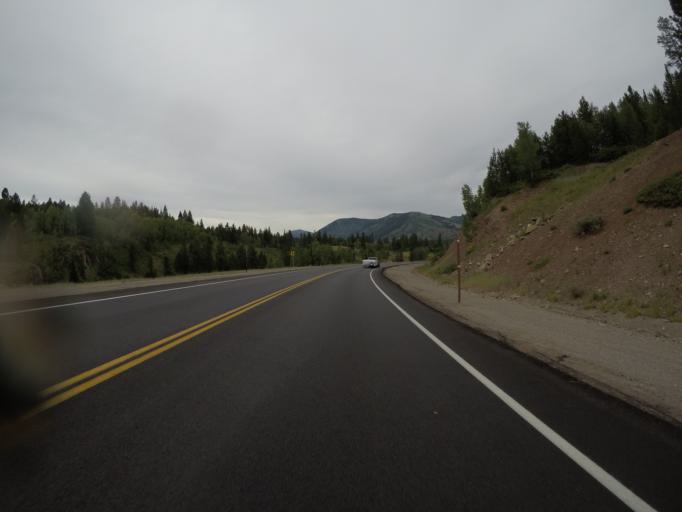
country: US
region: Wyoming
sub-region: Lincoln County
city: Afton
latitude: 42.5387
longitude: -110.8998
